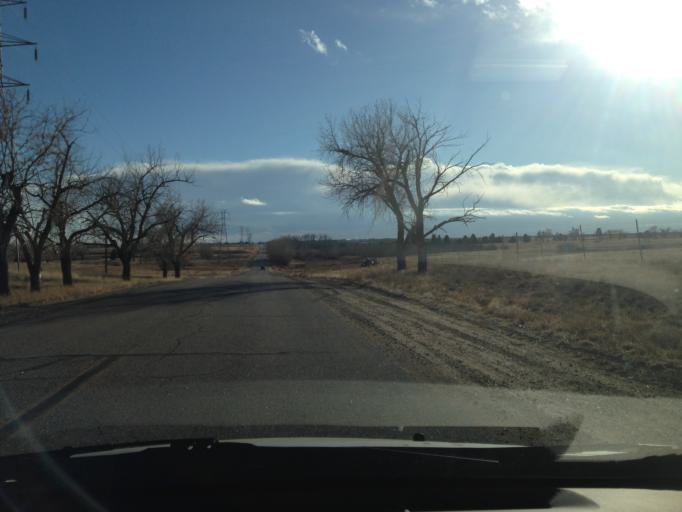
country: US
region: Colorado
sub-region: Adams County
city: Derby
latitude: 39.8237
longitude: -104.8658
